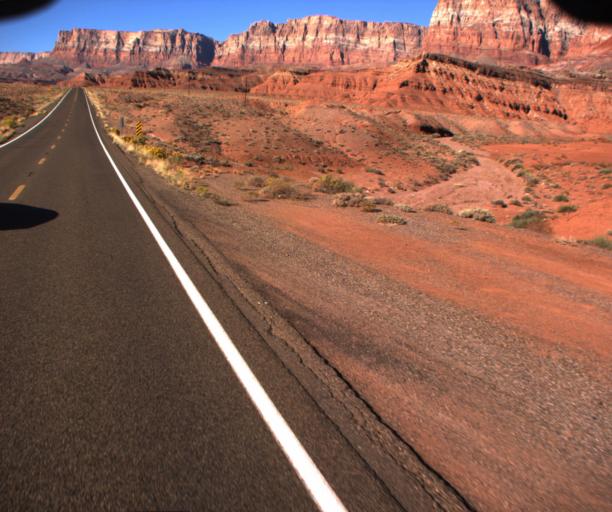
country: US
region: Arizona
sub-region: Coconino County
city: Page
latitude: 36.8117
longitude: -111.6576
